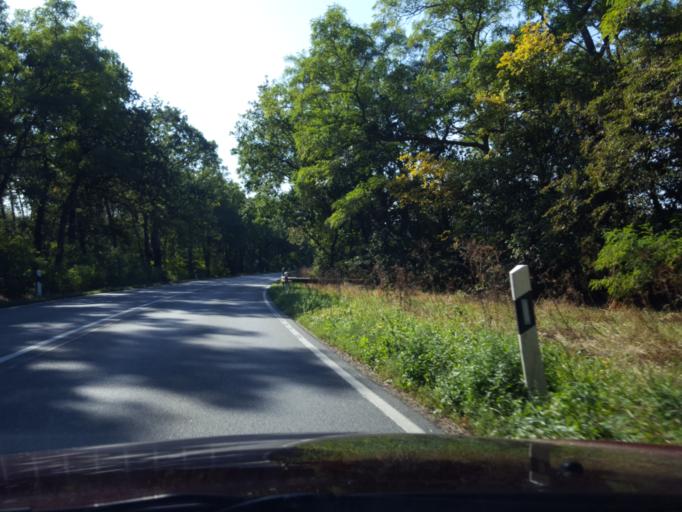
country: DE
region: Lower Saxony
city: Eystrup
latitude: 52.7953
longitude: 9.2122
